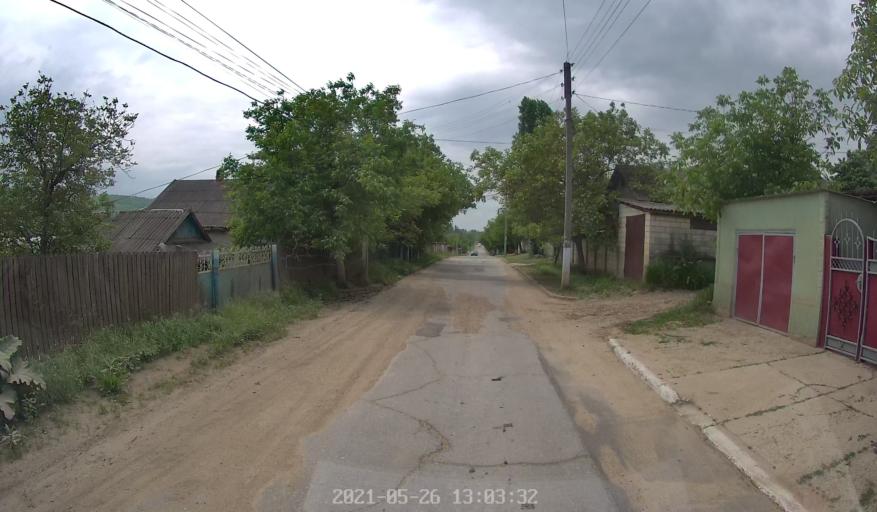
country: MD
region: Hincesti
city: Dancu
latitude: 46.7621
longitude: 28.3432
